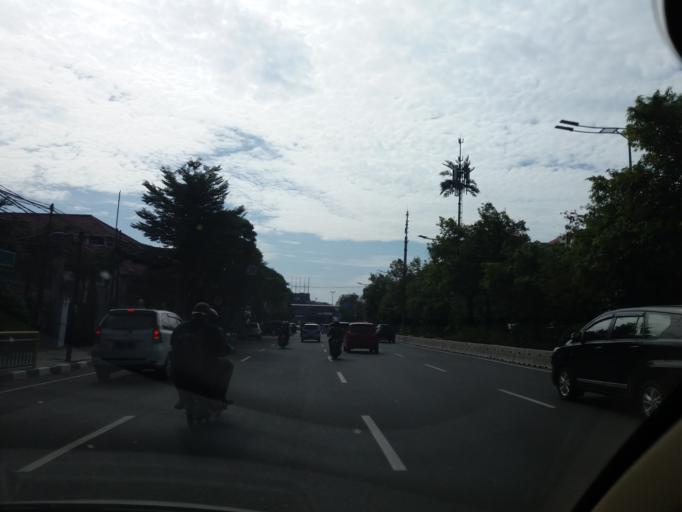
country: ID
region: Jakarta Raya
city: Jakarta
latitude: -6.1861
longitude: 106.8448
